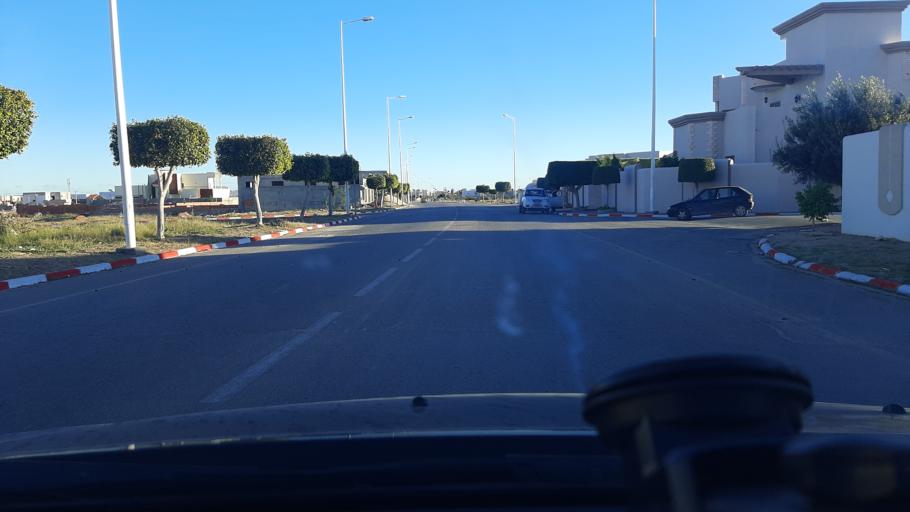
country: TN
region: Safaqis
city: Sfax
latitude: 34.8060
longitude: 10.7138
